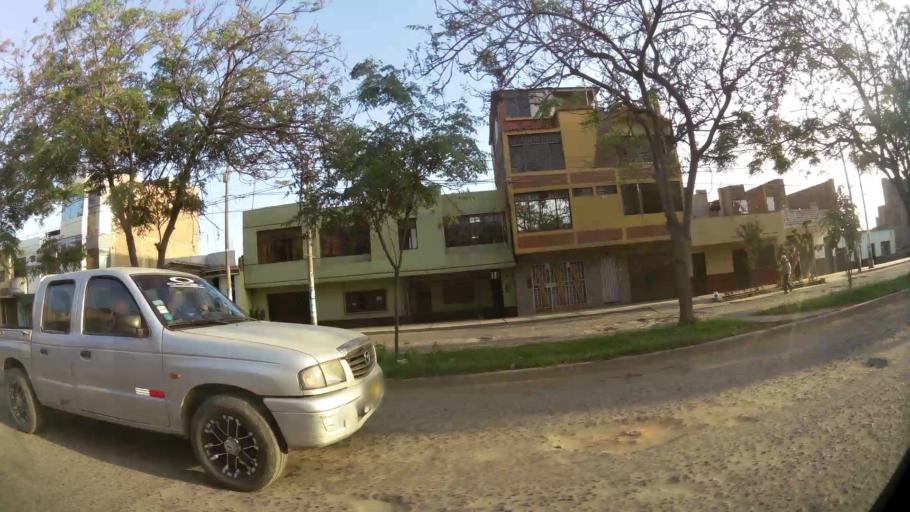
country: PE
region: La Libertad
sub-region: Provincia de Trujillo
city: El Porvenir
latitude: -8.0886
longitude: -78.9959
